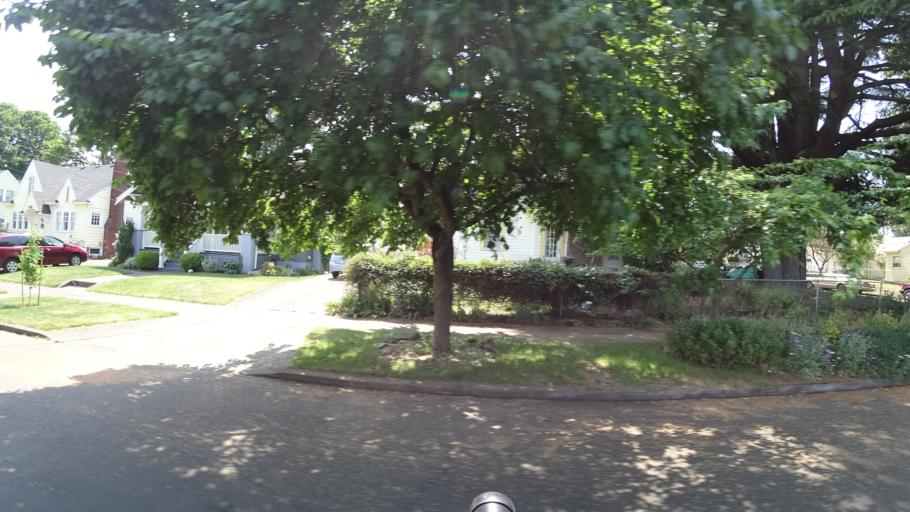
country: US
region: Oregon
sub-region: Multnomah County
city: Portland
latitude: 45.5810
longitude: -122.6843
